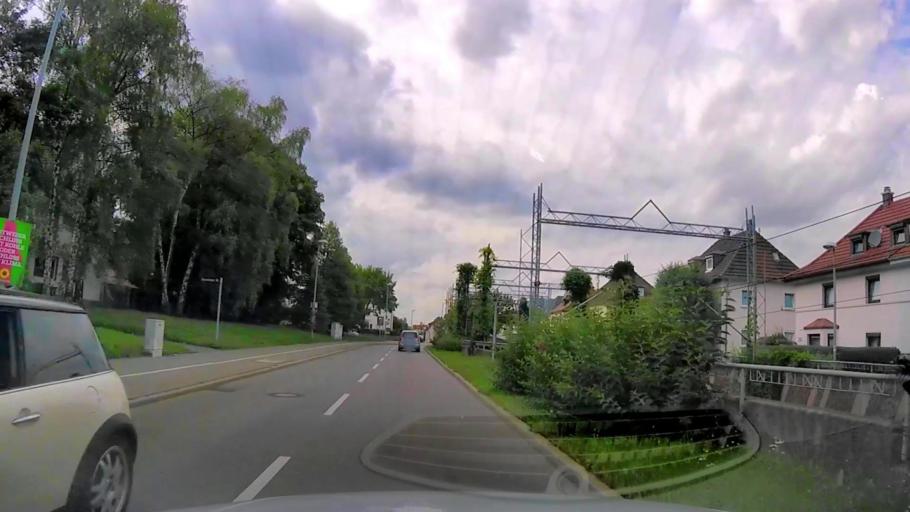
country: DE
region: Baden-Wuerttemberg
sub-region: Regierungsbezirk Stuttgart
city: Korntal
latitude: 48.8145
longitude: 9.1228
